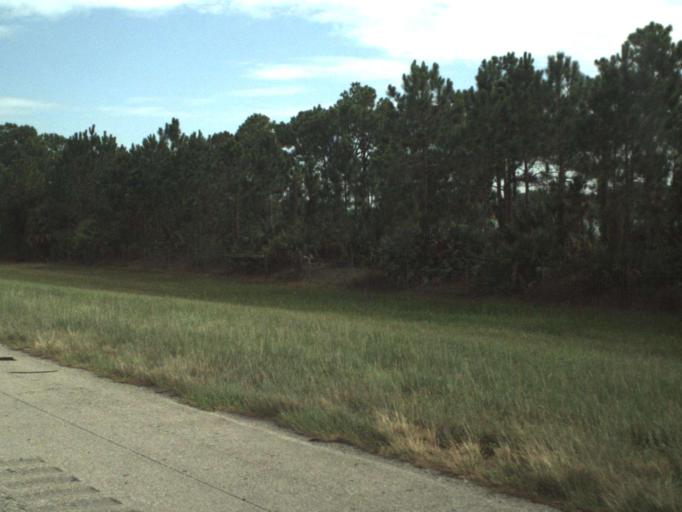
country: US
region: Florida
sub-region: Saint Lucie County
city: Port Saint Lucie
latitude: 27.2369
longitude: -80.4094
